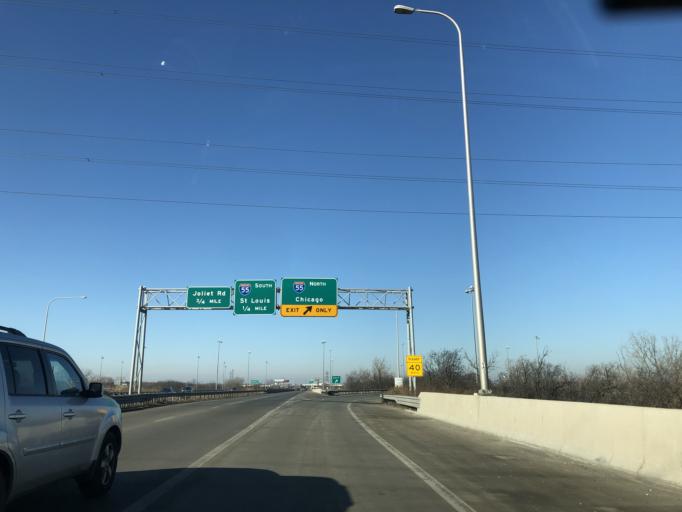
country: US
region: Illinois
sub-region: Cook County
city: Summit
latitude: 41.7914
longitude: -87.8147
